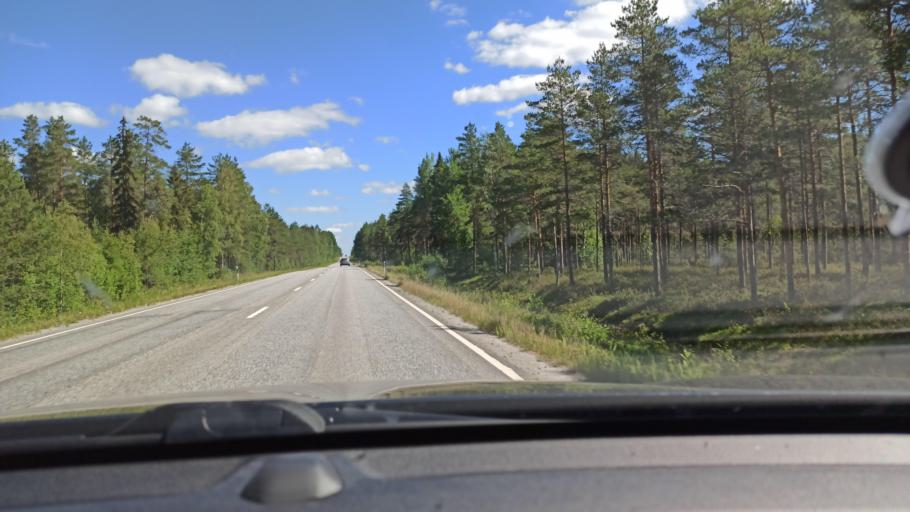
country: FI
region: Ostrobothnia
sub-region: Vaasa
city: Malax
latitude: 62.9779
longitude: 21.6111
